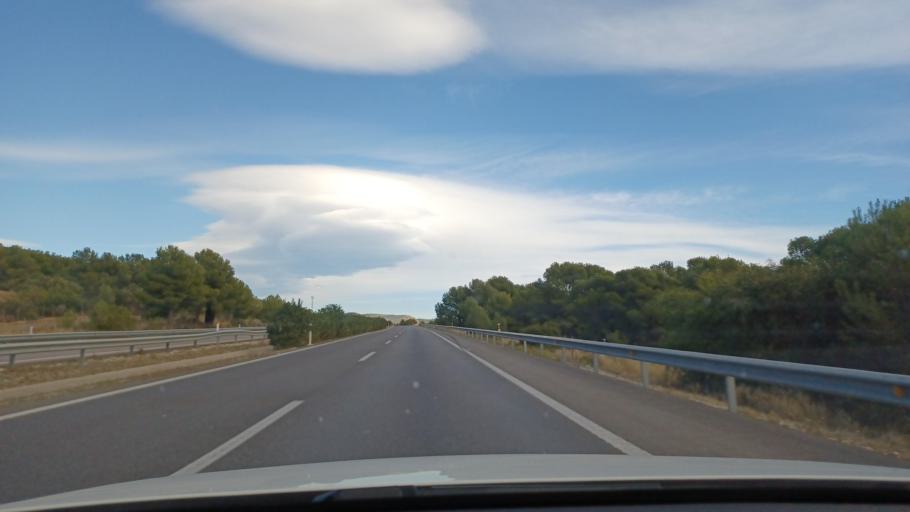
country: ES
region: Valencia
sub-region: Provincia de Castello
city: Benicassim
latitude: 40.0383
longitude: 0.0170
